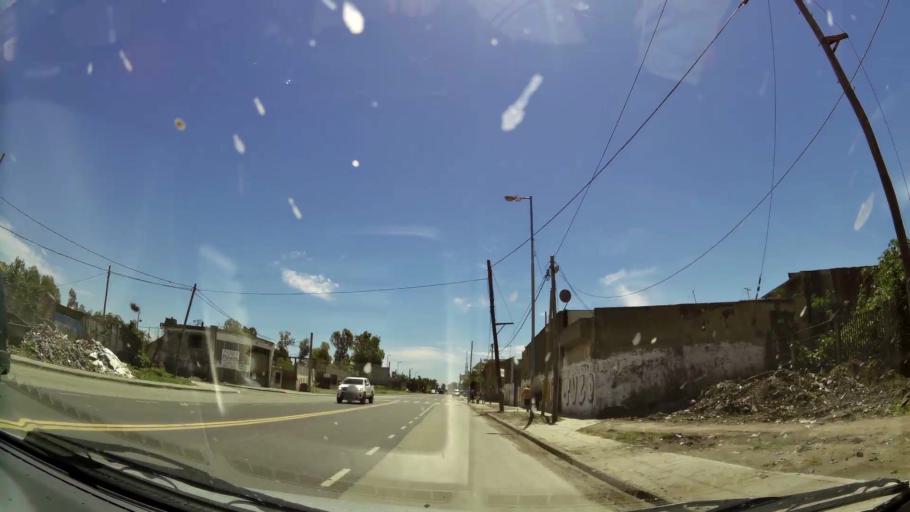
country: AR
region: Buenos Aires
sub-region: Partido de Quilmes
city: Quilmes
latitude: -34.7417
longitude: -58.3166
